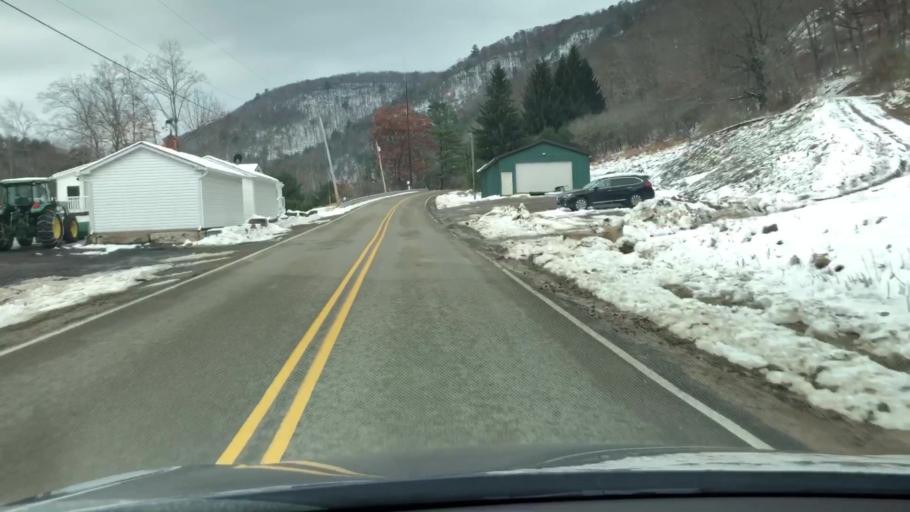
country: US
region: Pennsylvania
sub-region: Cameron County
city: Emporium
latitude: 41.3428
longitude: -78.2836
